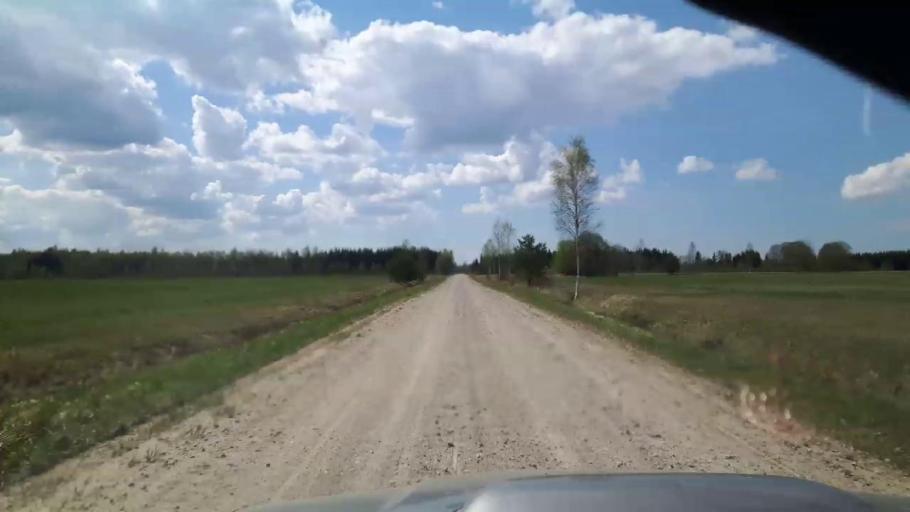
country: EE
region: Paernumaa
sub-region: Tootsi vald
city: Tootsi
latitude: 58.4604
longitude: 24.8831
